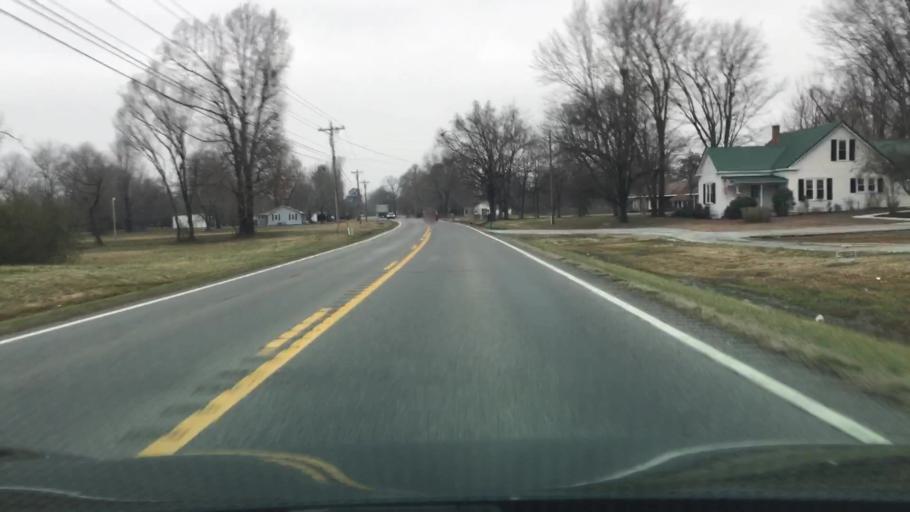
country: US
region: Kentucky
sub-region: Marshall County
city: Calvert City
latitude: 36.9685
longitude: -88.3864
